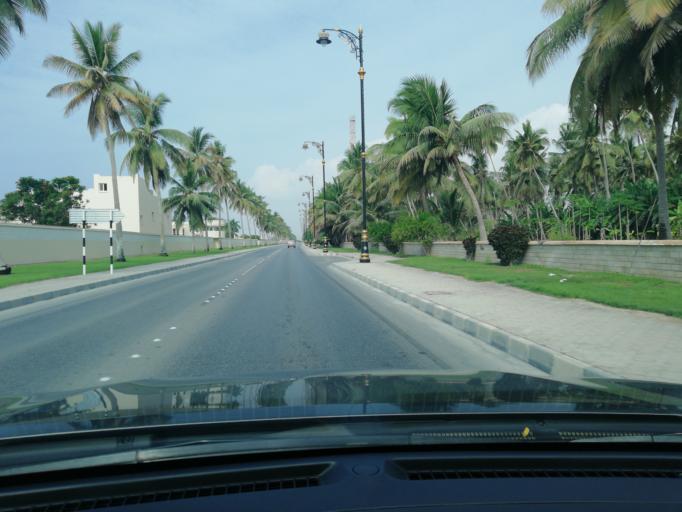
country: OM
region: Zufar
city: Salalah
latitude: 17.0001
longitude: 54.0874
